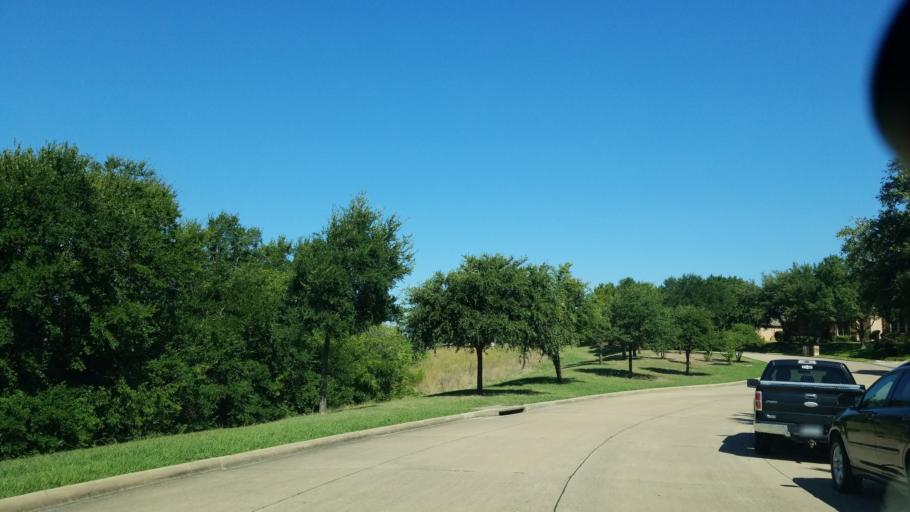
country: US
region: Texas
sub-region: Dallas County
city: Carrollton
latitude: 32.9672
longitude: -96.8855
